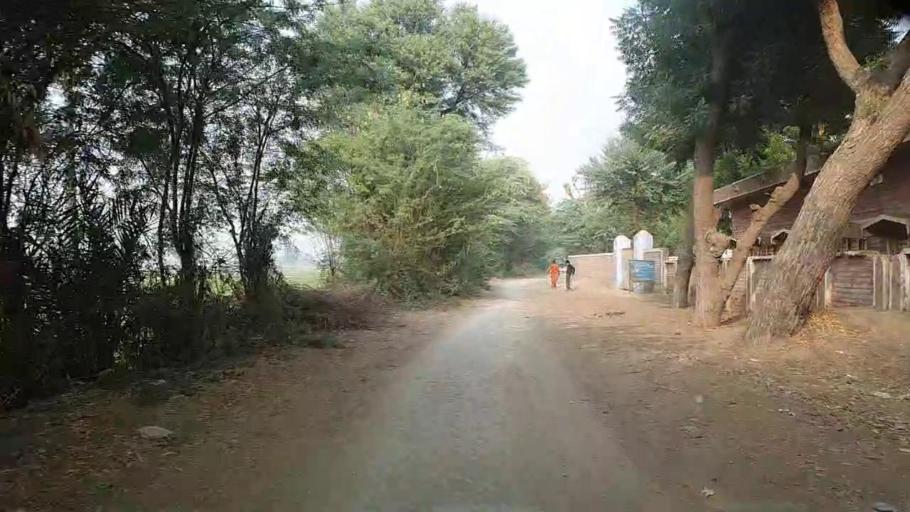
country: PK
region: Sindh
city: Bozdar
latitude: 27.1379
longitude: 68.6618
